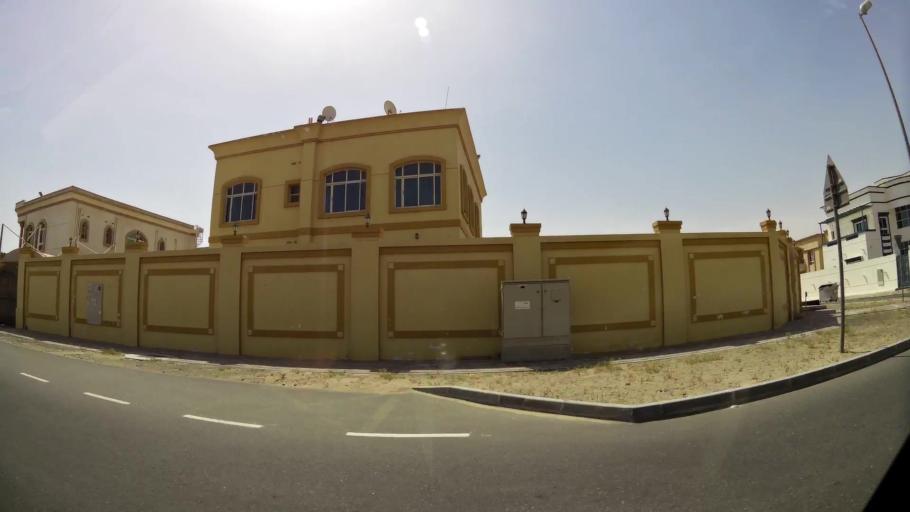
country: AE
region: Ash Shariqah
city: Sharjah
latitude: 25.2045
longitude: 55.4237
